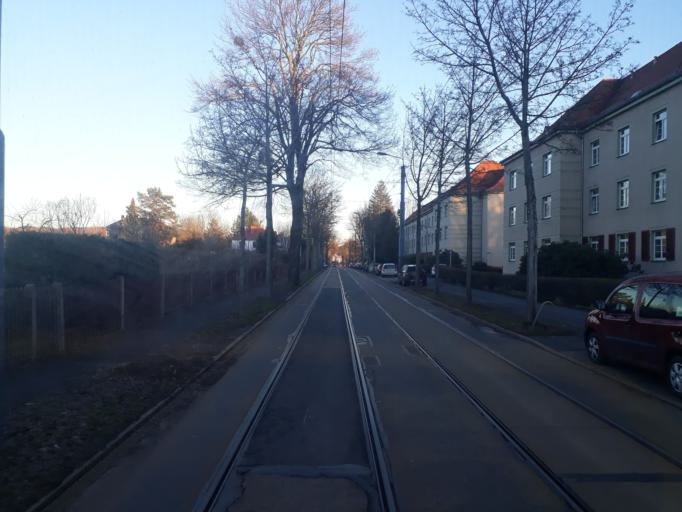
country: DE
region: Saxony
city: Heidenau
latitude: 51.0086
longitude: 13.8412
